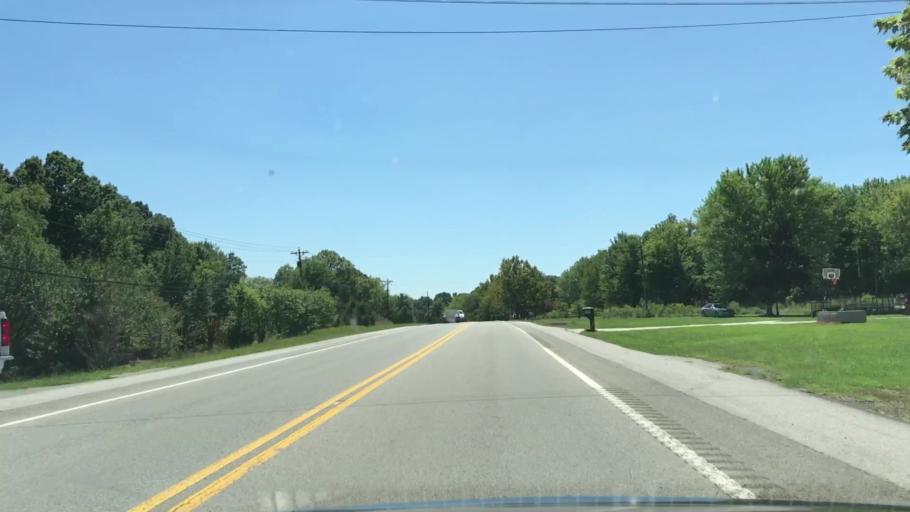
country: US
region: Tennessee
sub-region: Jackson County
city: Gainesboro
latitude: 36.2732
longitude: -85.6178
